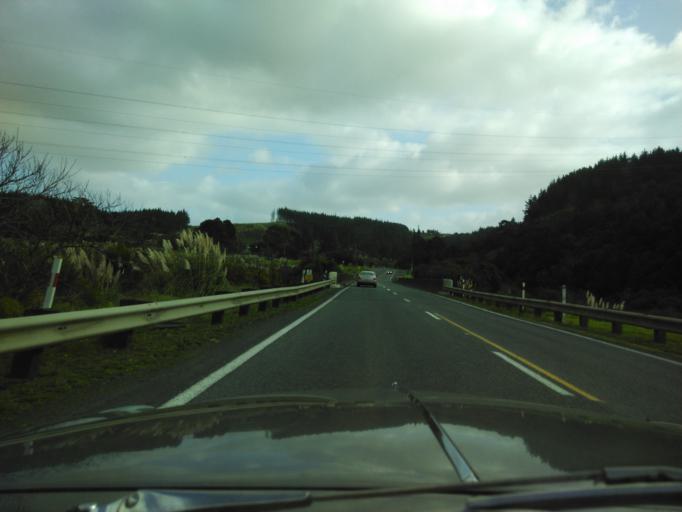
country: NZ
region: Auckland
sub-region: Auckland
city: Wellsford
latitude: -36.2122
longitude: 174.4711
